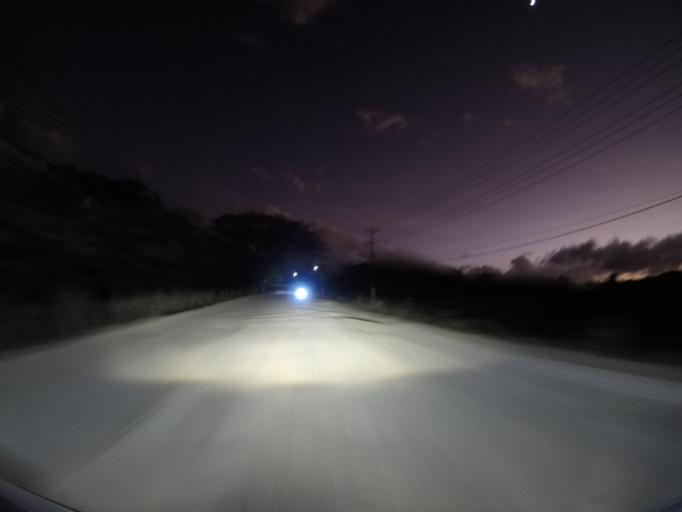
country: TL
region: Lautem
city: Lospalos
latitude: -8.4527
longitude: 127.0002
